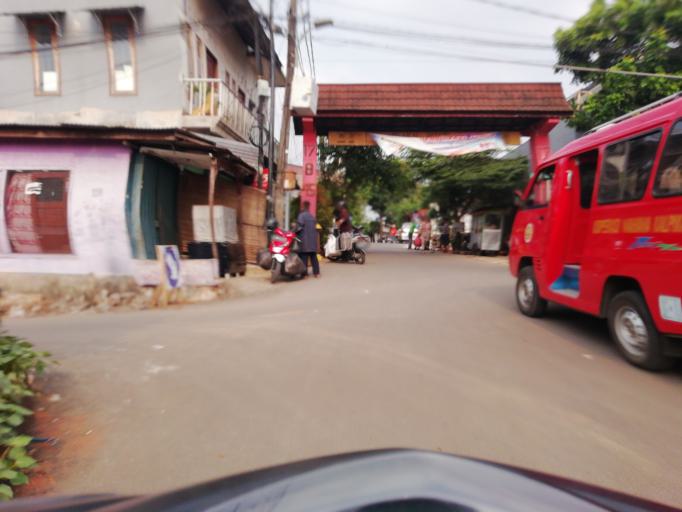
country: ID
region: West Java
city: Pamulang
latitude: -6.3029
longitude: 106.8044
